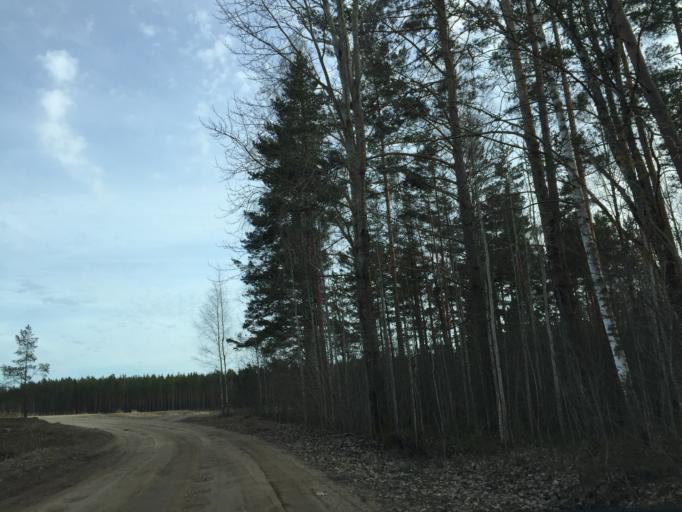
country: EE
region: Paernumaa
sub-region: Paernu linn
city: Parnu
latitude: 58.2138
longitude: 24.4976
